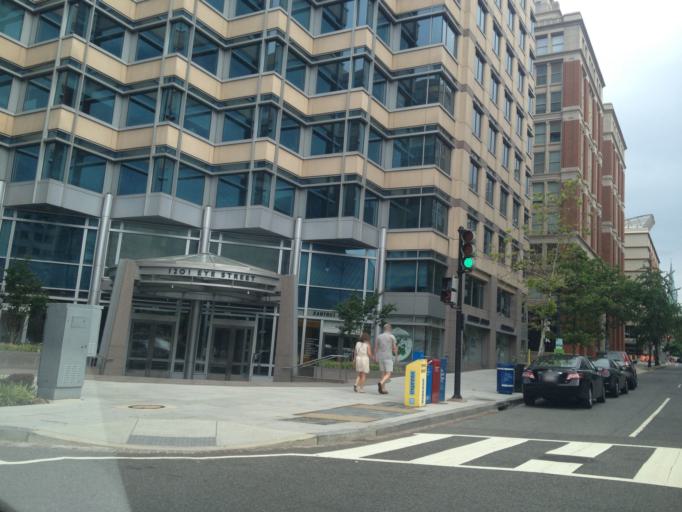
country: US
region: Washington, D.C.
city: Washington, D.C.
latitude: 38.9013
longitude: -77.0282
